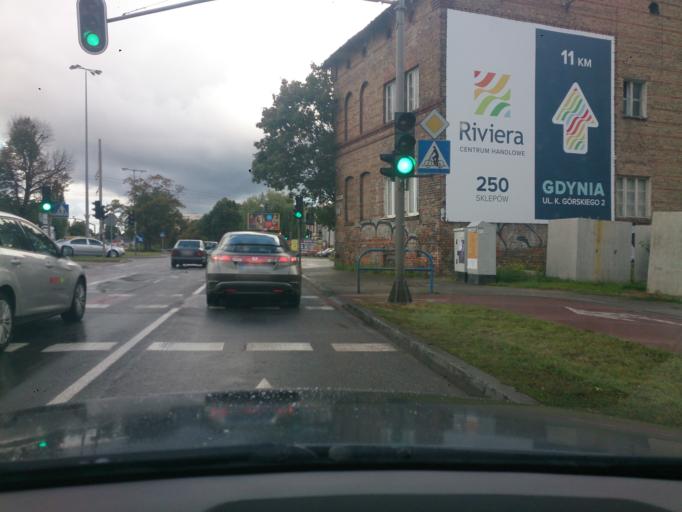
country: PL
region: Pomeranian Voivodeship
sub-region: Sopot
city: Sopot
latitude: 54.4136
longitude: 18.5665
